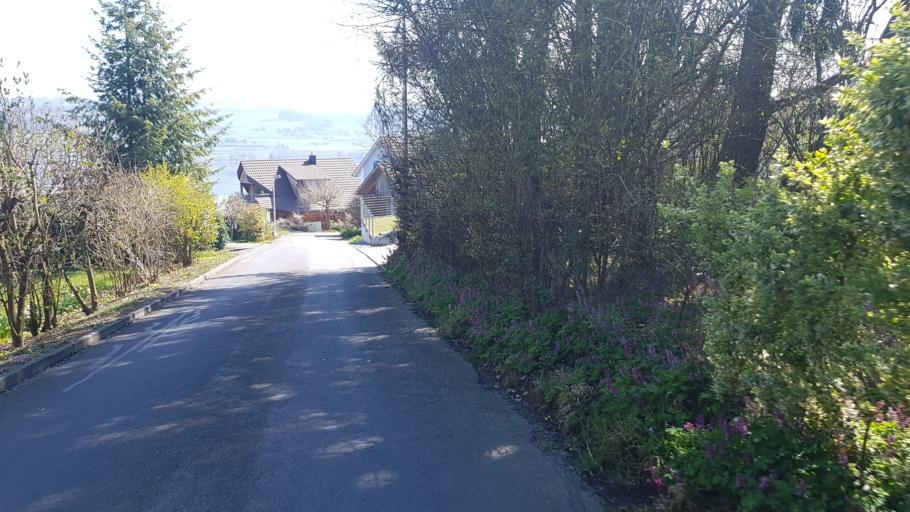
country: CH
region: Aargau
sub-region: Bezirk Kulm
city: Reinach
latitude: 47.2664
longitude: 8.2060
